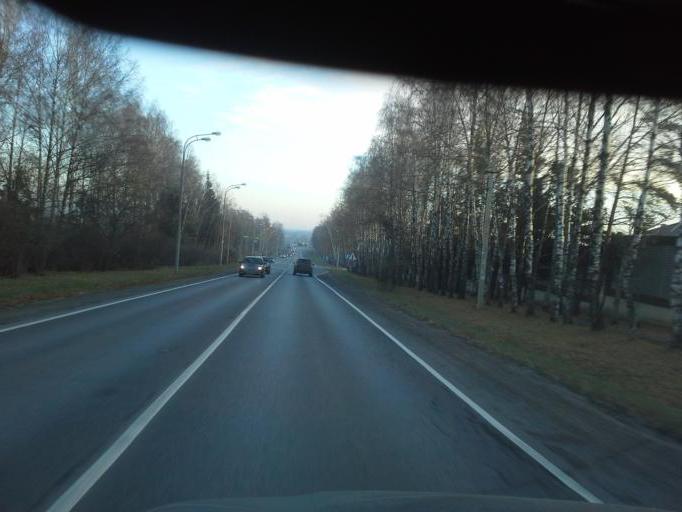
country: RU
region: Moskovskaya
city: Zhavoronki
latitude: 55.6016
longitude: 37.1093
